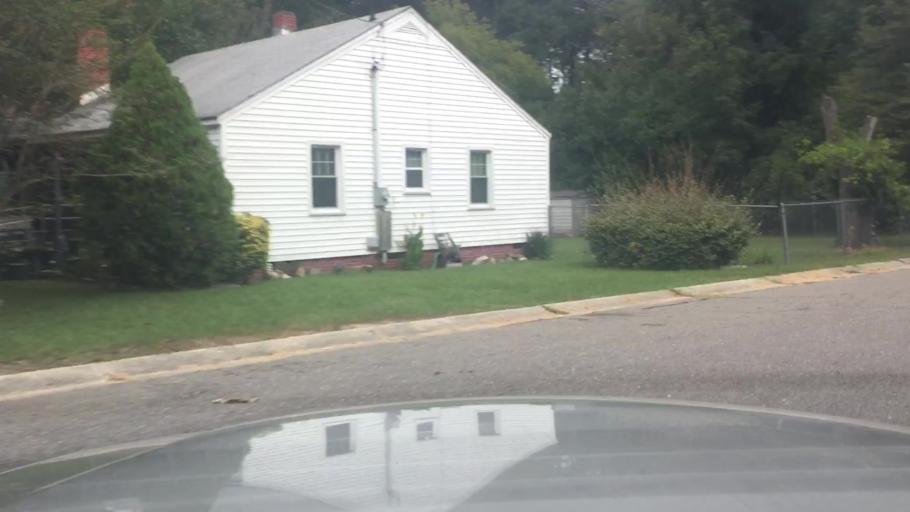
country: US
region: North Carolina
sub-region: Cumberland County
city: Fayetteville
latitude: 35.0747
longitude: -78.8869
